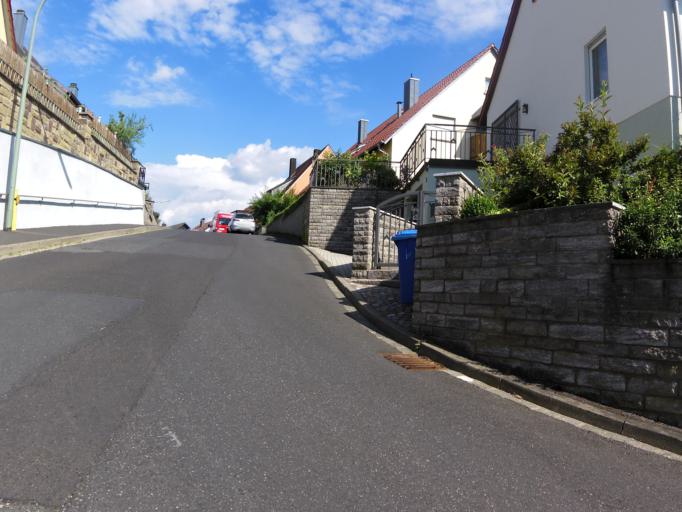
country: DE
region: Bavaria
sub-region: Regierungsbezirk Unterfranken
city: Wuerzburg
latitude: 49.8241
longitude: 9.9650
